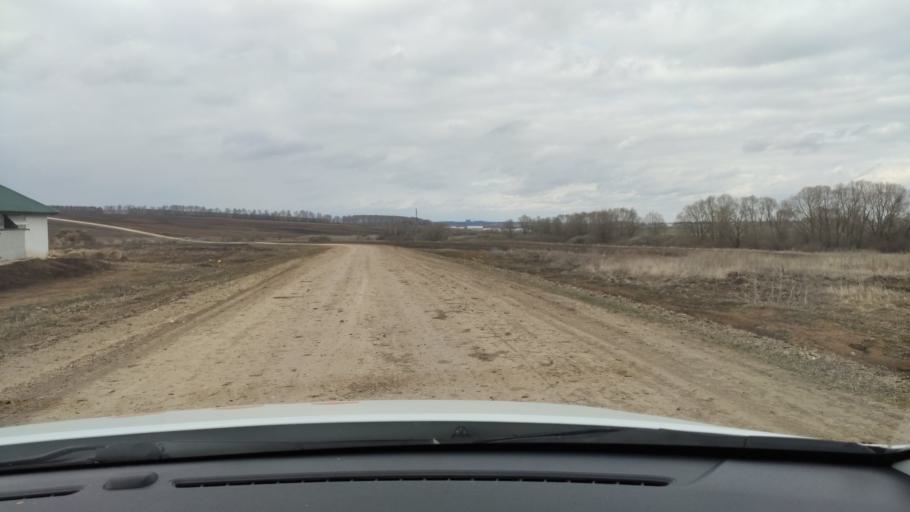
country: RU
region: Tatarstan
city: Vysokaya Gora
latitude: 56.2180
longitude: 49.3134
